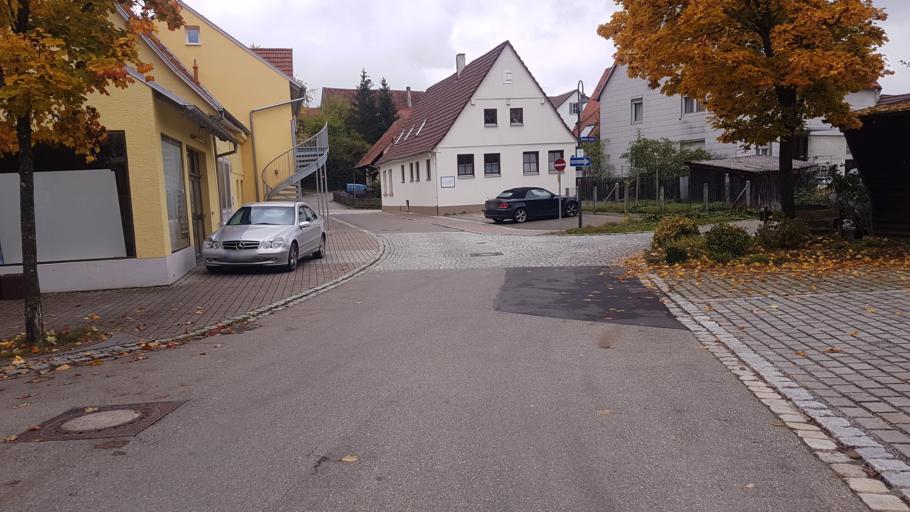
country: DE
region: Baden-Wuerttemberg
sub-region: Tuebingen Region
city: Dusslingen
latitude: 48.4476
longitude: 9.0553
